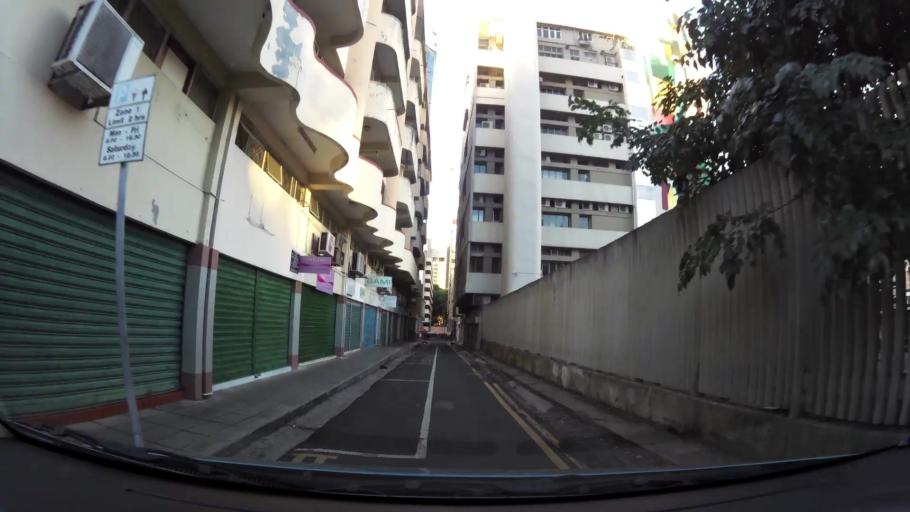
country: MU
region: Port Louis
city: Port Louis
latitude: -20.1649
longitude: 57.5004
